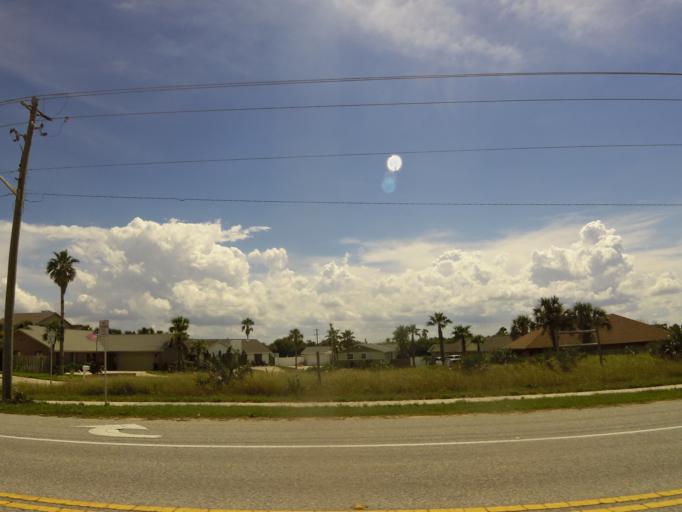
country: US
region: Florida
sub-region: Volusia County
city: Ormond-by-the-Sea
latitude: 29.3796
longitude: -81.0809
